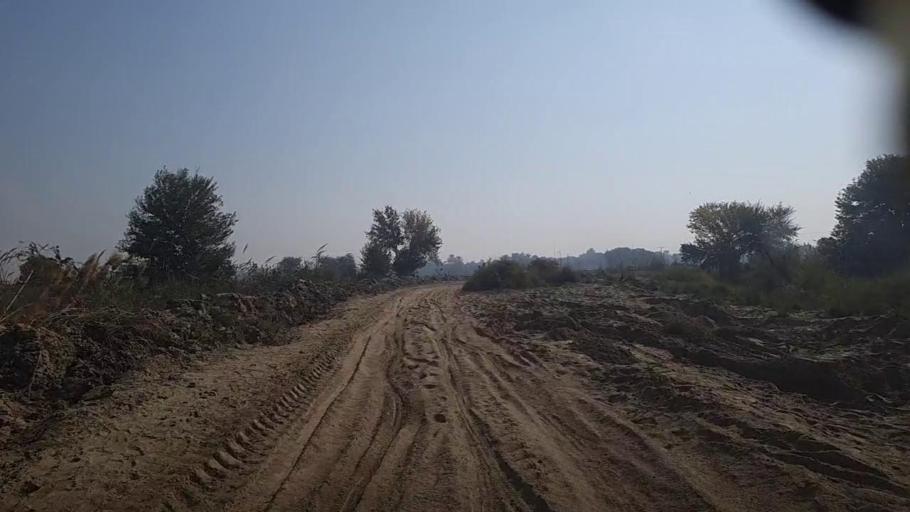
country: PK
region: Sindh
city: Kandiari
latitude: 27.0125
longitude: 68.5024
